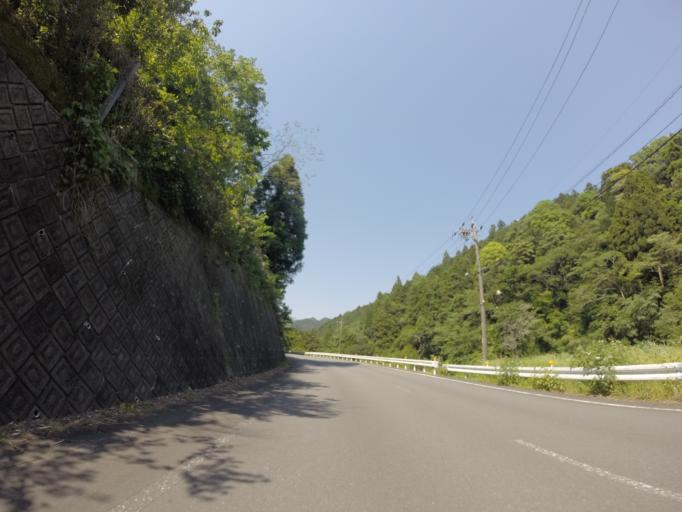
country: JP
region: Shizuoka
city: Fujinomiya
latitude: 35.1418
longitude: 138.5603
